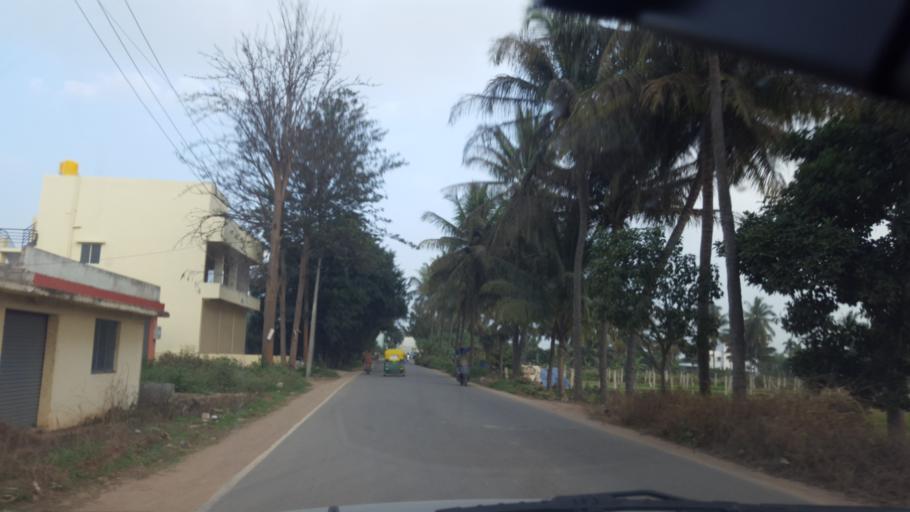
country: IN
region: Karnataka
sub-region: Bangalore Rural
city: Hoskote
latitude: 13.0527
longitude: 77.6972
